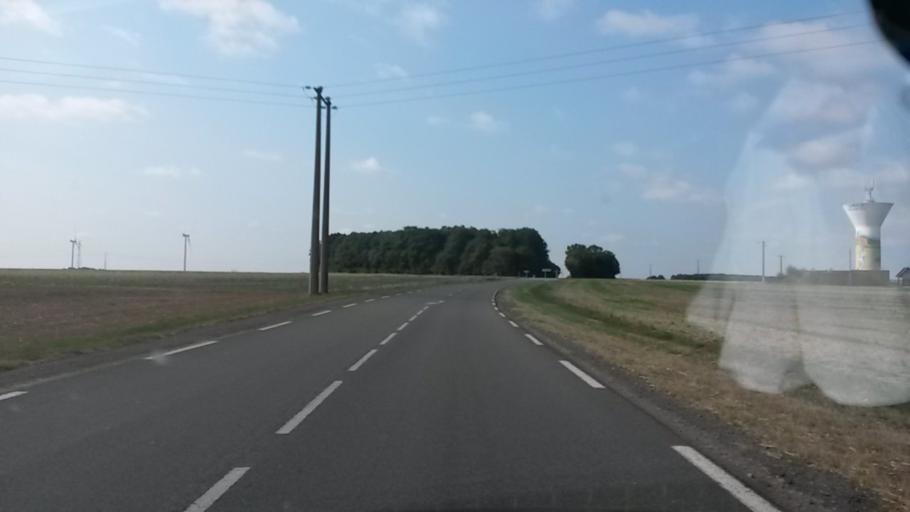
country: FR
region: Haute-Normandie
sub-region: Departement de l'Eure
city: Damville
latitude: 48.8582
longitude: 1.0642
